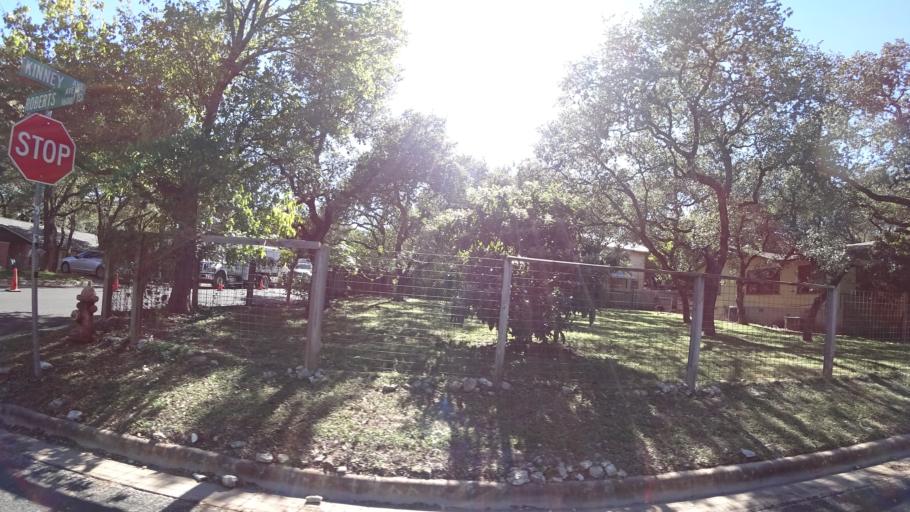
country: US
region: Texas
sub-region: Travis County
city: Rollingwood
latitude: 30.2397
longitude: -97.7752
